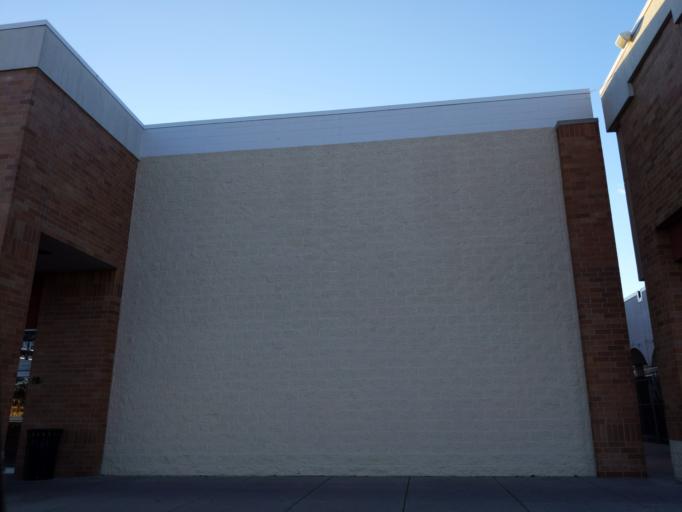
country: US
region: Michigan
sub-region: Ingham County
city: East Lansing
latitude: 42.7382
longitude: -84.5070
